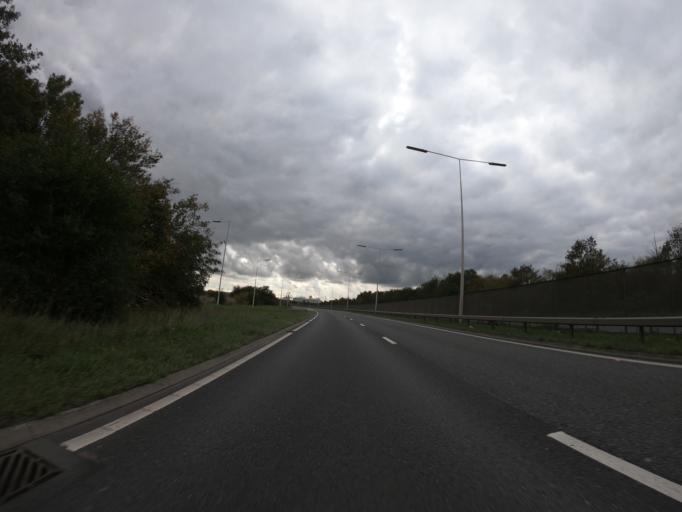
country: GB
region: England
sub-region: Borough of Thurrock
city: Chadwell St Mary
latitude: 51.4783
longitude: 0.3502
